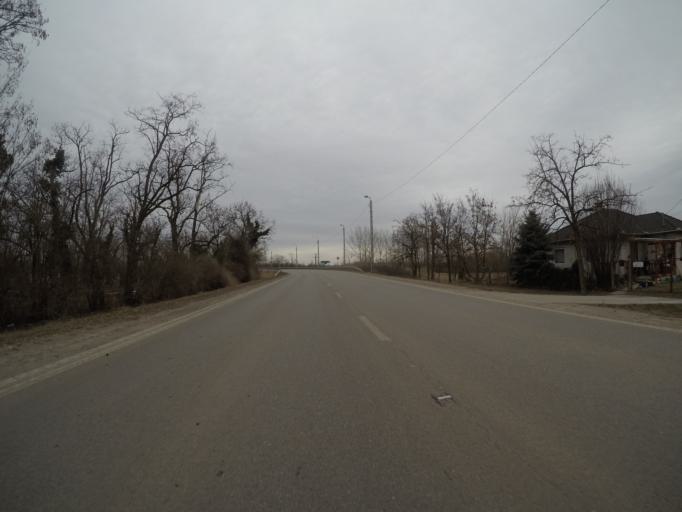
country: HU
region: Jasz-Nagykun-Szolnok
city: Jaszjakohalma
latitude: 47.5189
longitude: 20.0065
